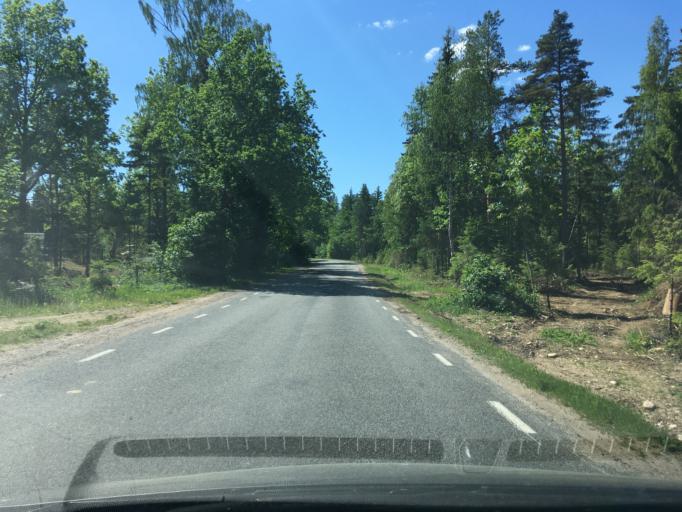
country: EE
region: Raplamaa
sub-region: Kohila vald
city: Kohila
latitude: 59.1148
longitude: 24.8298
